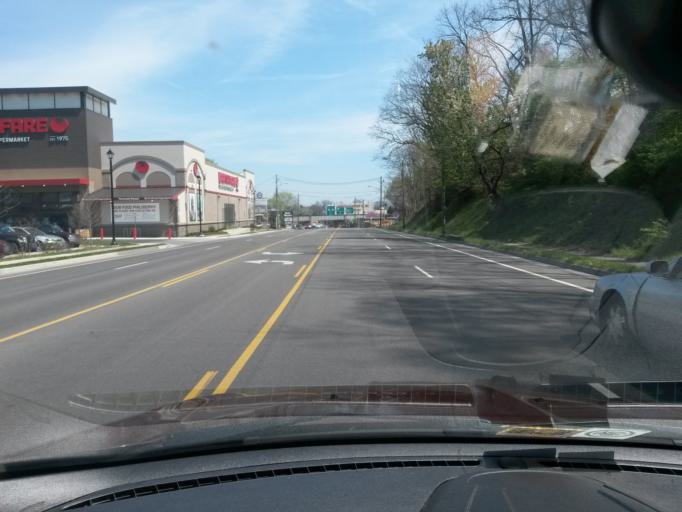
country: US
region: Virginia
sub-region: City of Roanoke
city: Cedar Bluff
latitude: 37.2511
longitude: -79.9539
